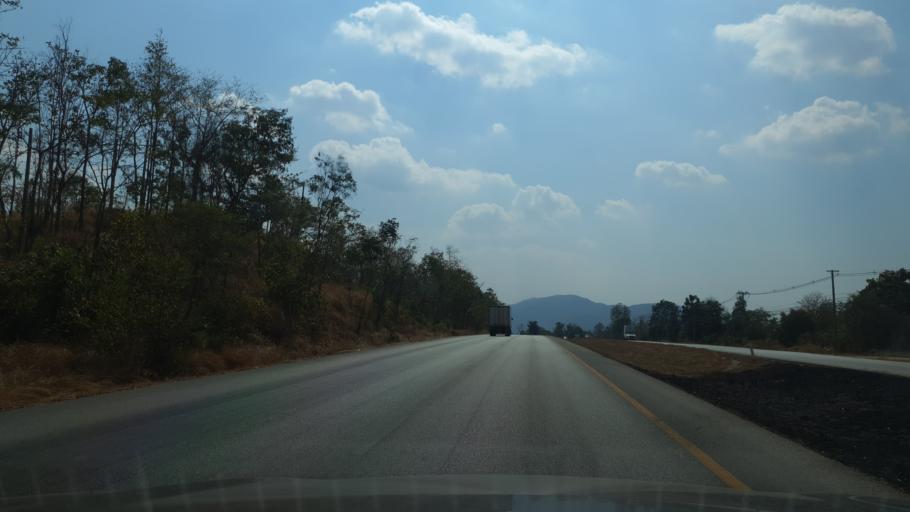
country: TH
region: Lampang
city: Mae Phrik
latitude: 17.3860
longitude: 99.1483
